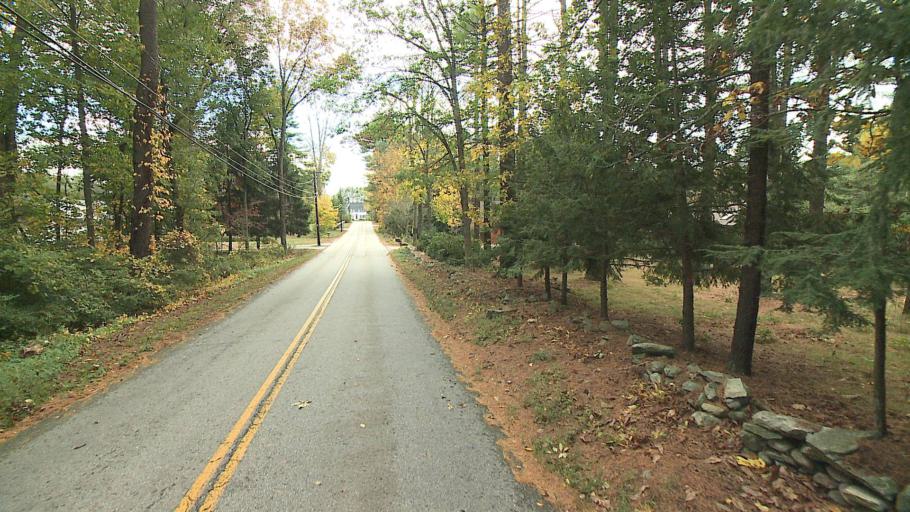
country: US
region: Connecticut
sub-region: Windham County
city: Thompson
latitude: 41.9401
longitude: -71.8206
